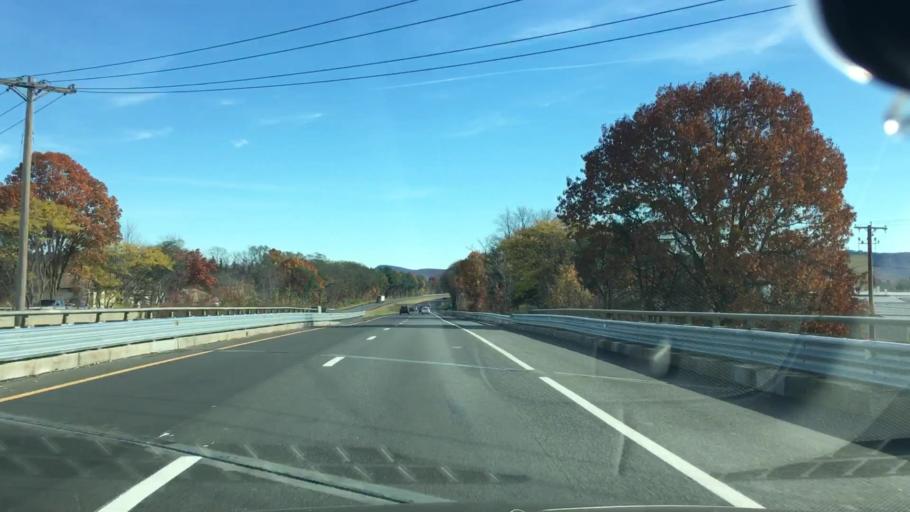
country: US
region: Massachusetts
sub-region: Hampshire County
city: Northampton
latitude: 42.3387
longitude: -72.6342
